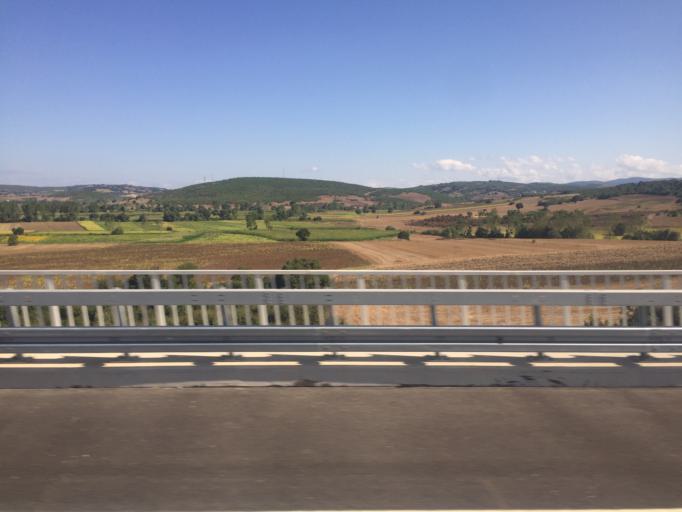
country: TR
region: Bursa
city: Mahmudiye
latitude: 40.2634
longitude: 28.6685
